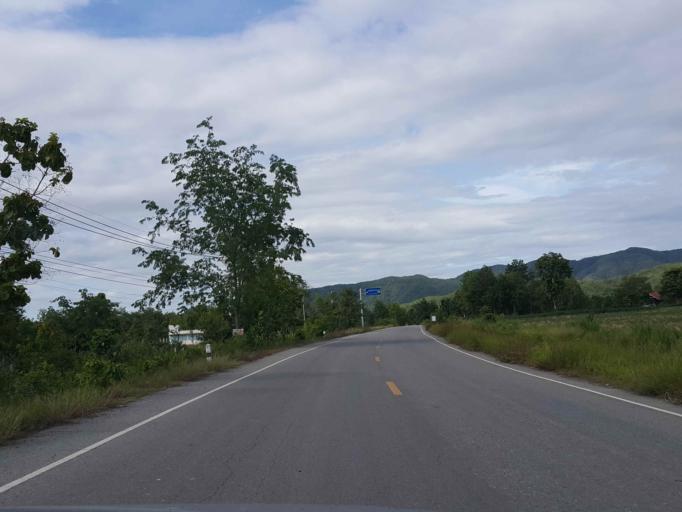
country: TH
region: Sukhothai
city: Thung Saliam
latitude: 17.2354
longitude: 99.5149
